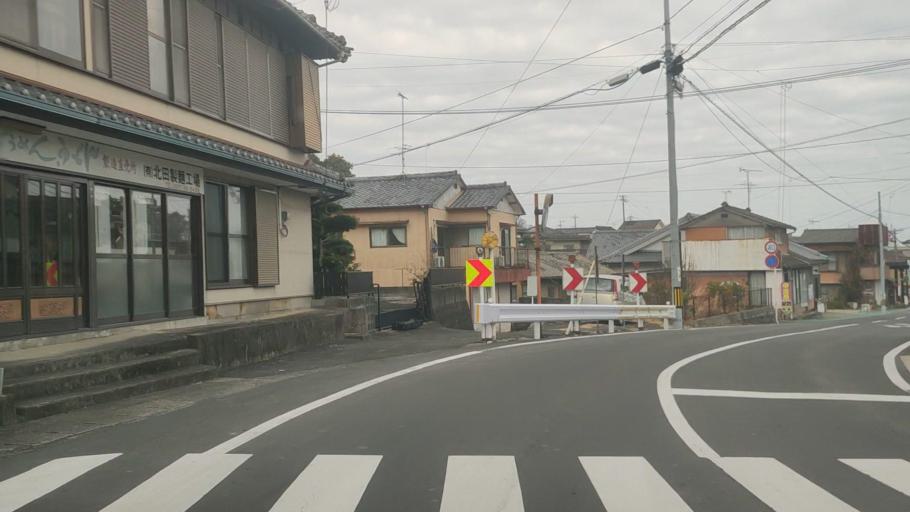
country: JP
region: Nagasaki
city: Shimabara
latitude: 32.7649
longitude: 130.3683
